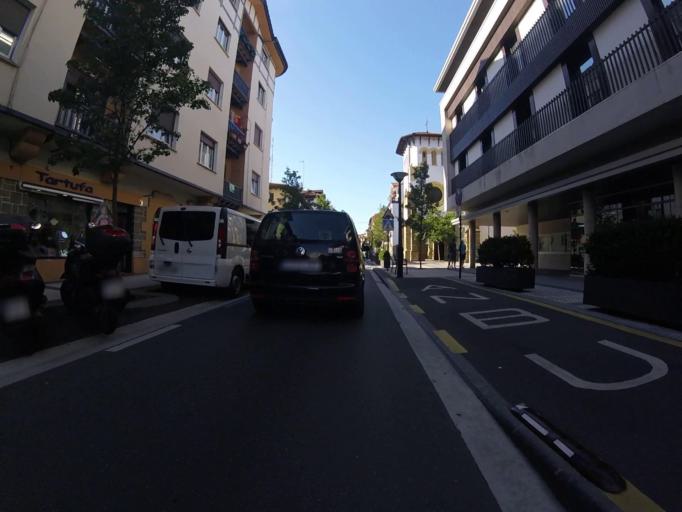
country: ES
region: Basque Country
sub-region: Provincia de Guipuzcoa
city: Fuenterrabia
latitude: 43.3674
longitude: -1.7932
